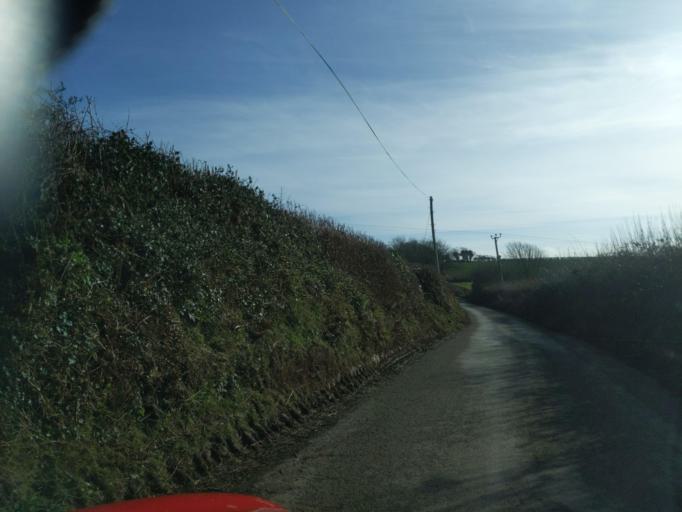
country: GB
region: England
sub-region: Devon
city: Kingsbridge
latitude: 50.3324
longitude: -3.7197
